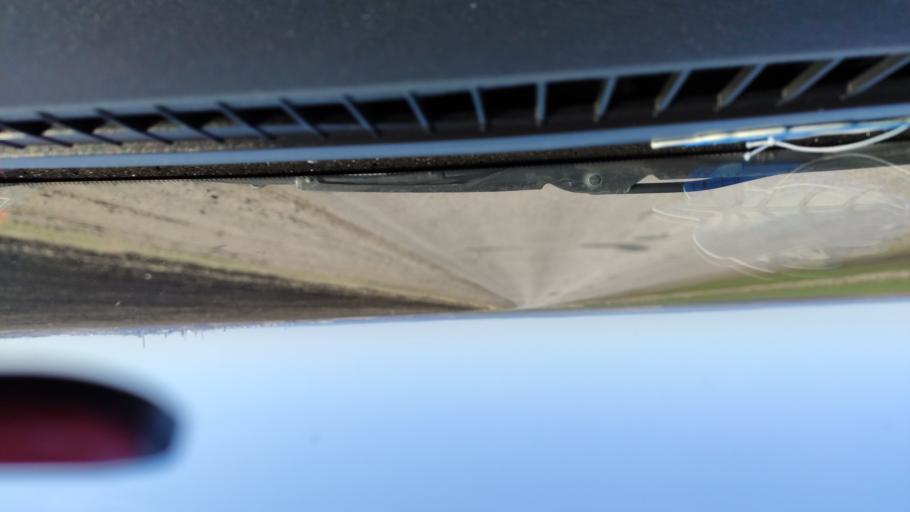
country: RU
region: Samara
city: Varlamovo
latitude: 53.0245
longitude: 48.3336
